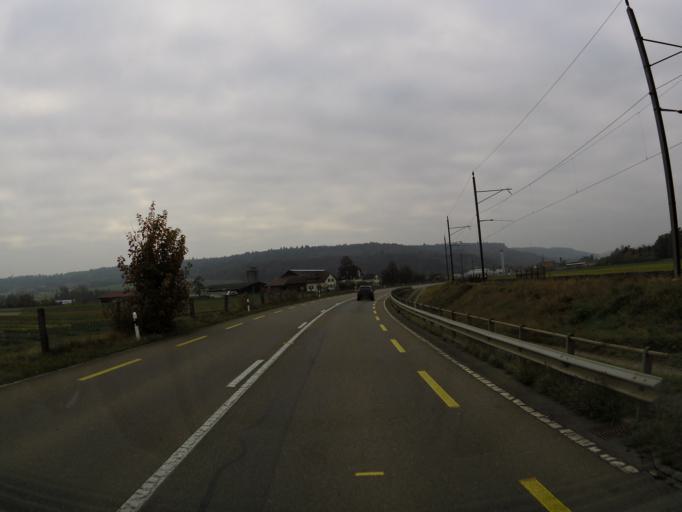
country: DE
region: Baden-Wuerttemberg
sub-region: Freiburg Region
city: Busingen
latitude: 47.6794
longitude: 8.7026
